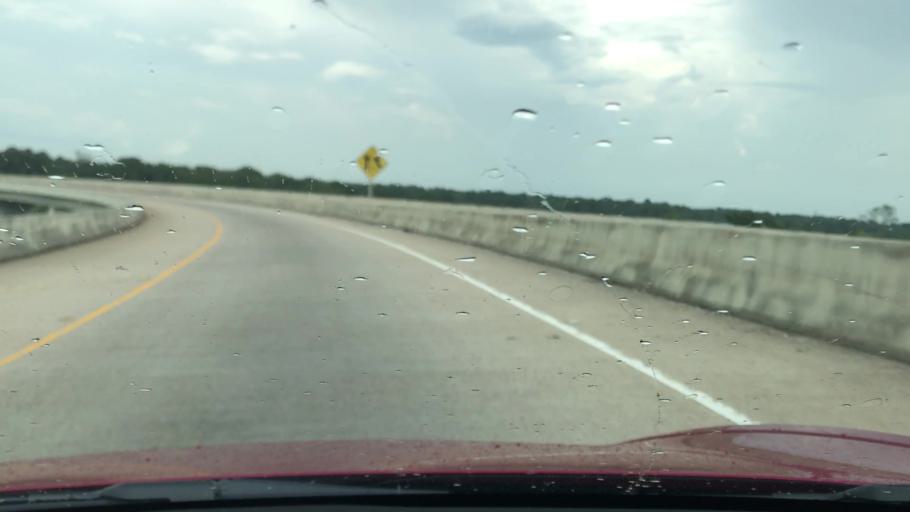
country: US
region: Louisiana
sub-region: Bossier Parish
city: Bossier City
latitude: 32.4200
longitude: -93.7487
